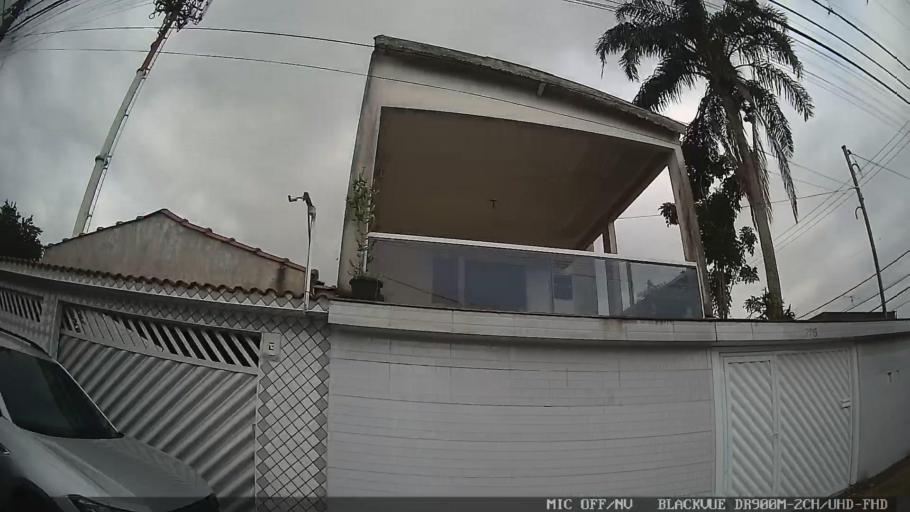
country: BR
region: Sao Paulo
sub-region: Santos
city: Santos
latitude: -23.9443
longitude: -46.2877
